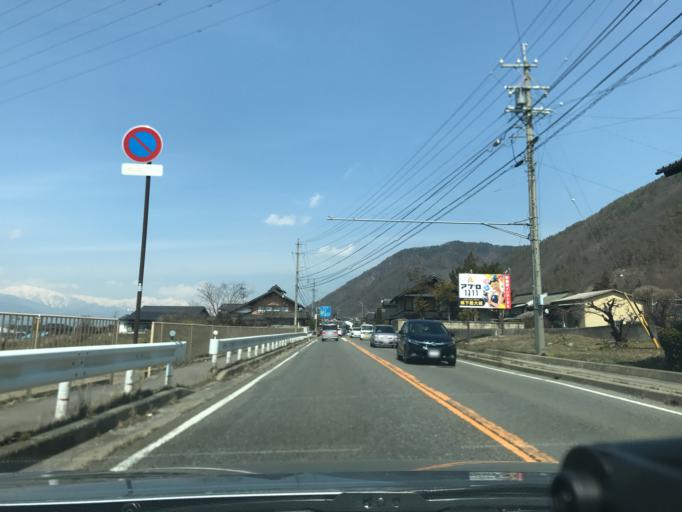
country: JP
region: Nagano
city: Toyoshina
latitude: 36.2991
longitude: 137.9407
